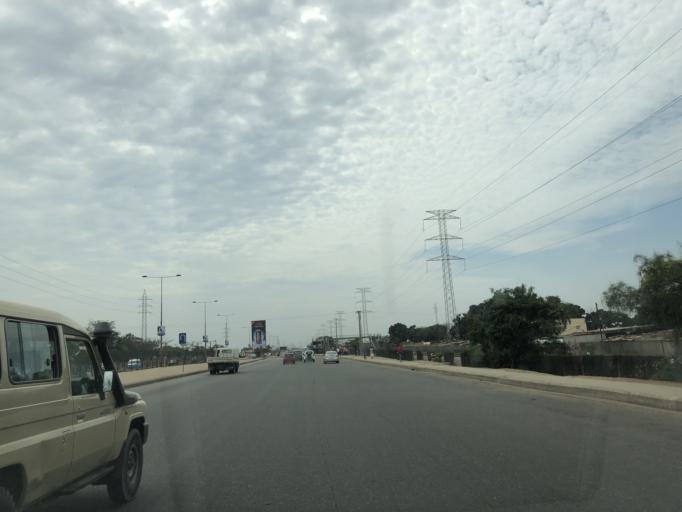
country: AO
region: Luanda
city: Luanda
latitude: -8.8636
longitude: 13.3086
